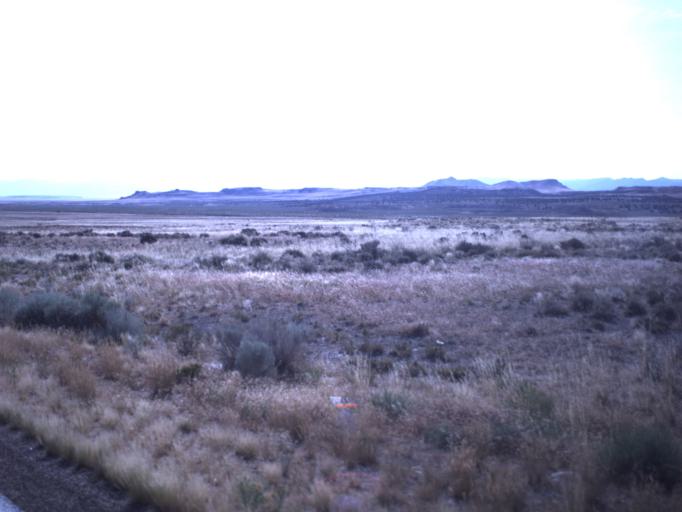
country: US
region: Utah
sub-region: Beaver County
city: Milford
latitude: 38.8086
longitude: -112.8758
